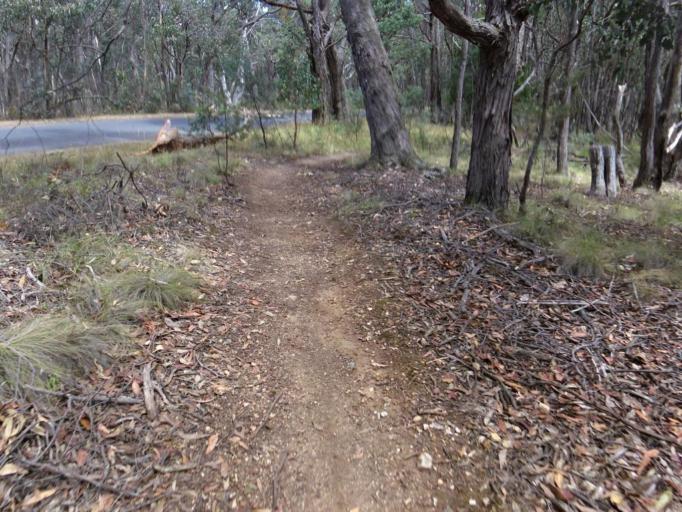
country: AU
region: Victoria
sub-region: Melton
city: Melton West
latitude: -37.4911
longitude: 144.5491
